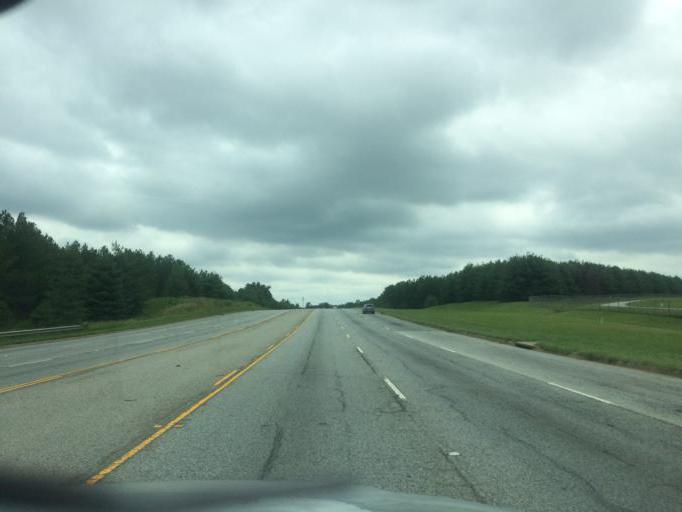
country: US
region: South Carolina
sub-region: Greenville County
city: Greer
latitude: 34.8831
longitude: -82.2319
